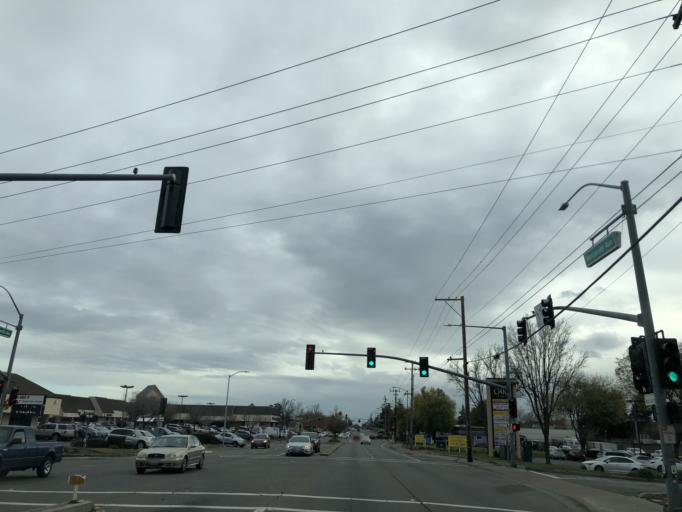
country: US
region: California
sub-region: Sacramento County
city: Carmichael
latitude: 38.6409
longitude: -121.3280
